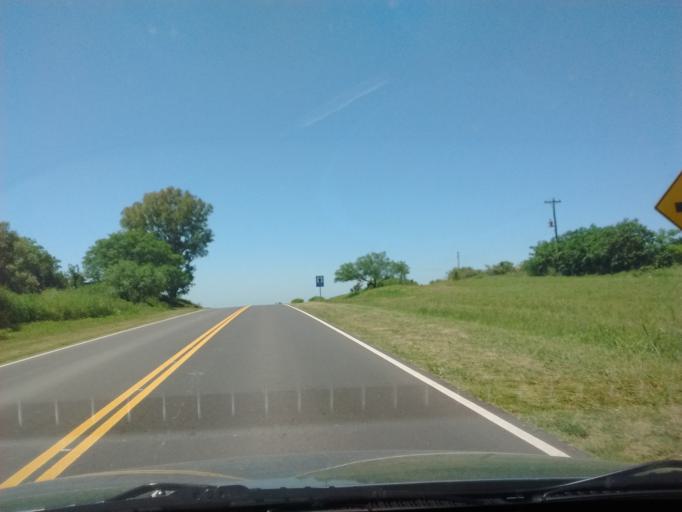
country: AR
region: Entre Rios
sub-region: Departamento de Victoria
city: Victoria
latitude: -32.8320
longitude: -59.8719
